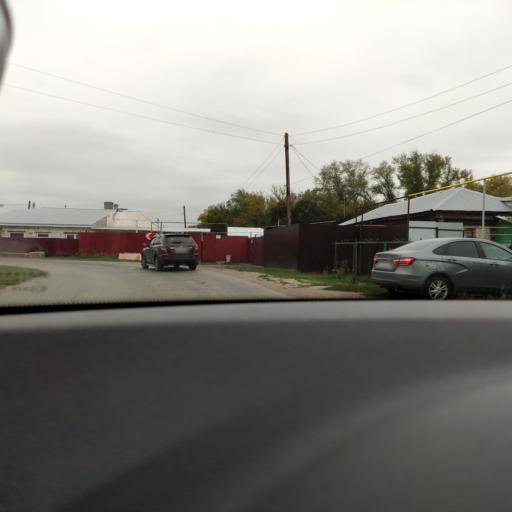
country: RU
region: Samara
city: Krasnyy Yar
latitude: 53.4907
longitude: 50.3853
